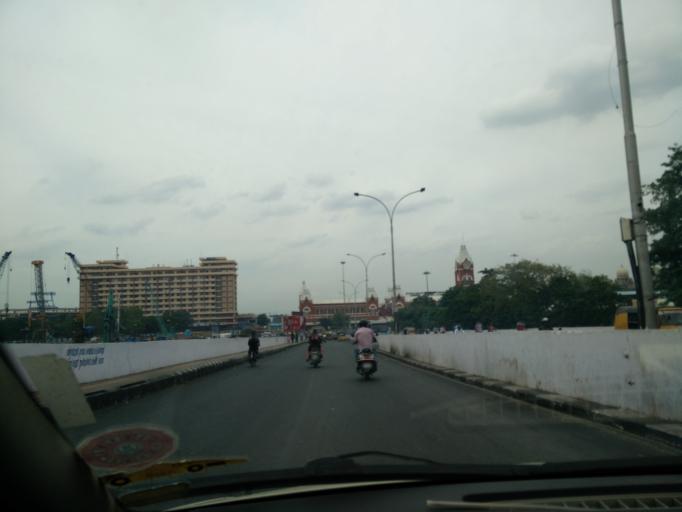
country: IN
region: Tamil Nadu
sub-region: Chennai
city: Chennai
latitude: 13.0799
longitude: 80.2753
